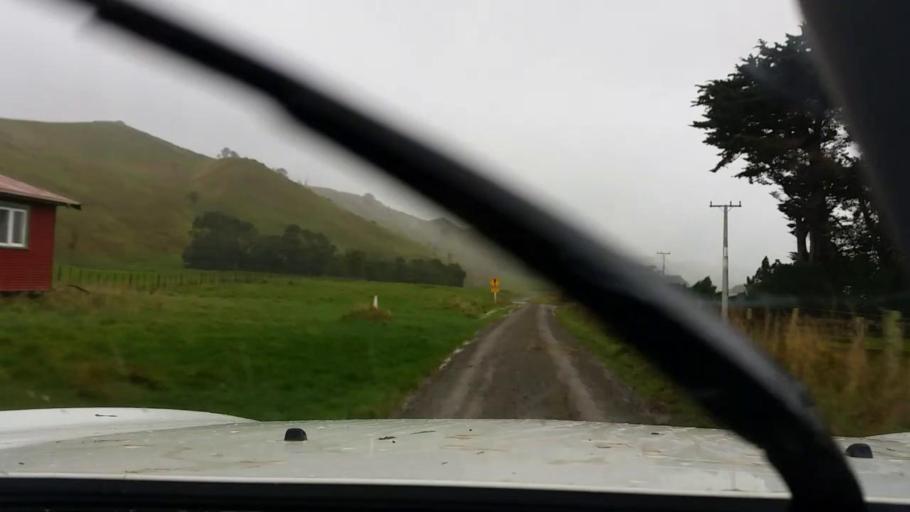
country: NZ
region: Wellington
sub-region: Masterton District
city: Masterton
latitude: -41.2621
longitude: 175.8951
